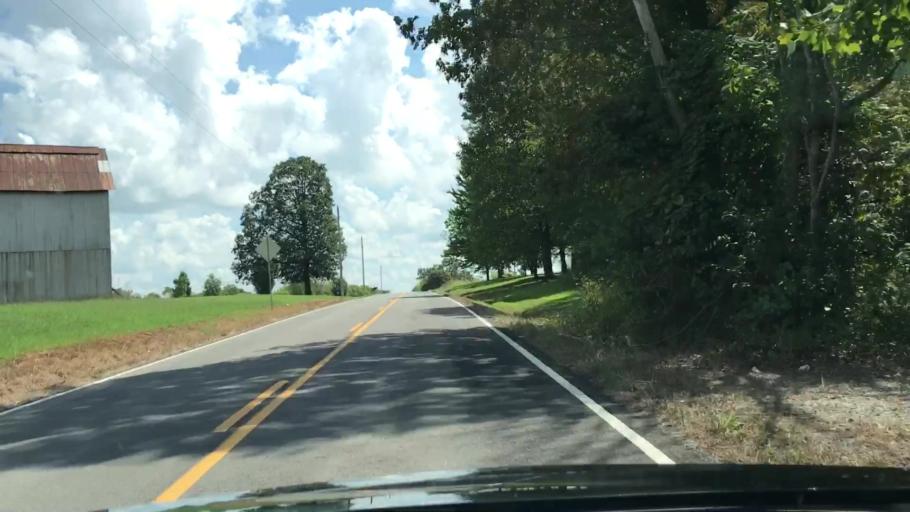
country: US
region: Tennessee
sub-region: Robertson County
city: Springfield
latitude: 36.5967
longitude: -86.9093
